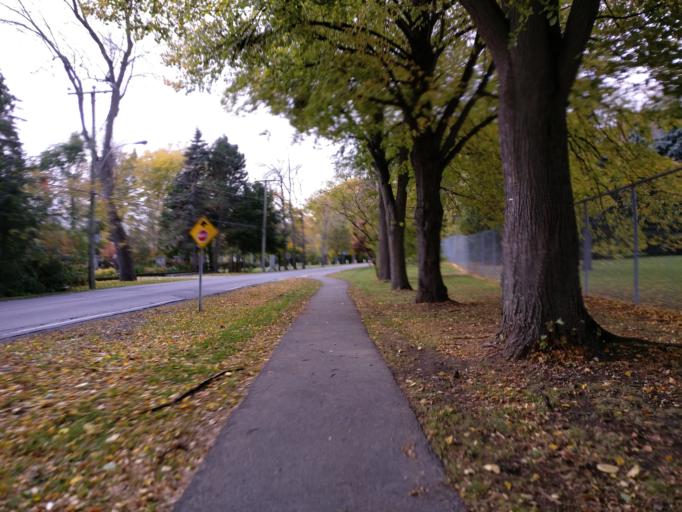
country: CA
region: Quebec
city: Baie-D'Urfe
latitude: 45.4054
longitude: -73.9220
